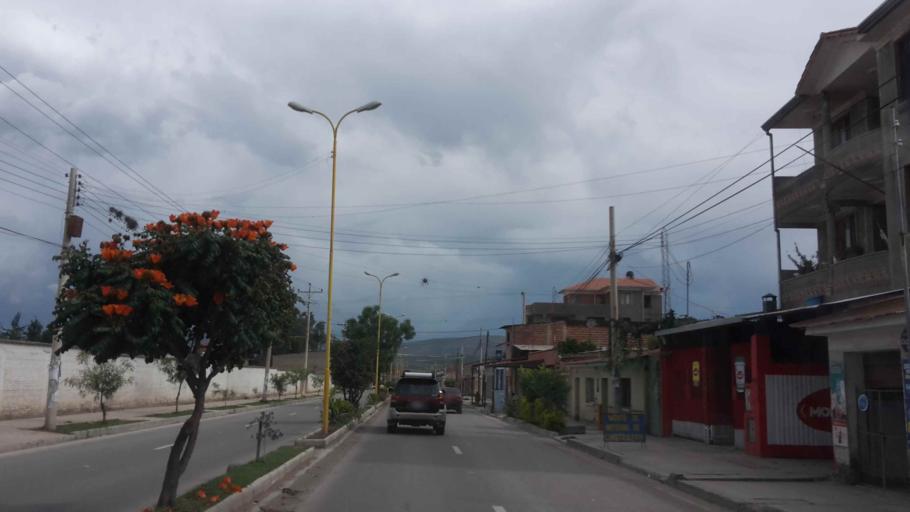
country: BO
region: Cochabamba
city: Cochabamba
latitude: -17.3832
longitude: -66.2510
